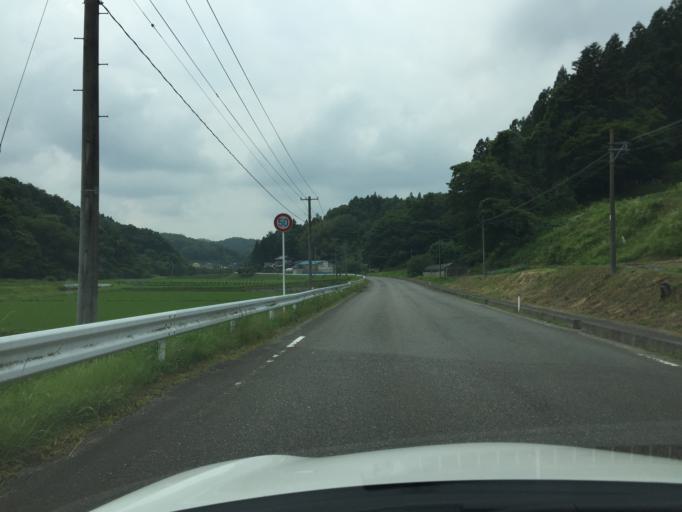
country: JP
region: Fukushima
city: Funehikimachi-funehiki
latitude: 37.2919
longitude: 140.5858
